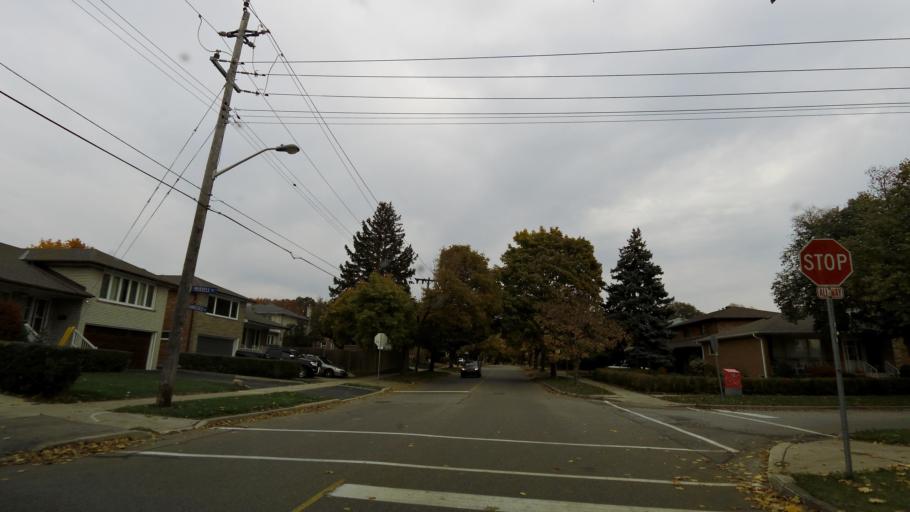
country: CA
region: Ontario
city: Etobicoke
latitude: 43.6845
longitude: -79.5344
